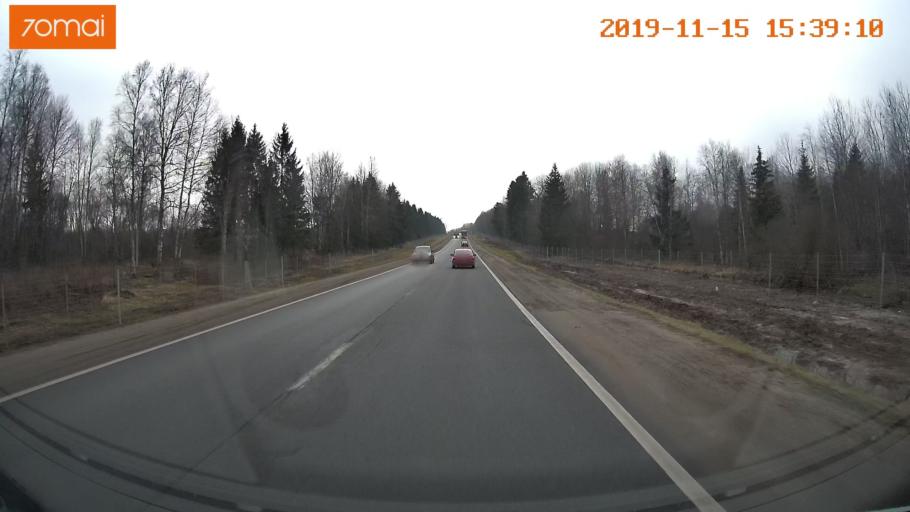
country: RU
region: Jaroslavl
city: Danilov
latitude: 58.0232
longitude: 40.0718
